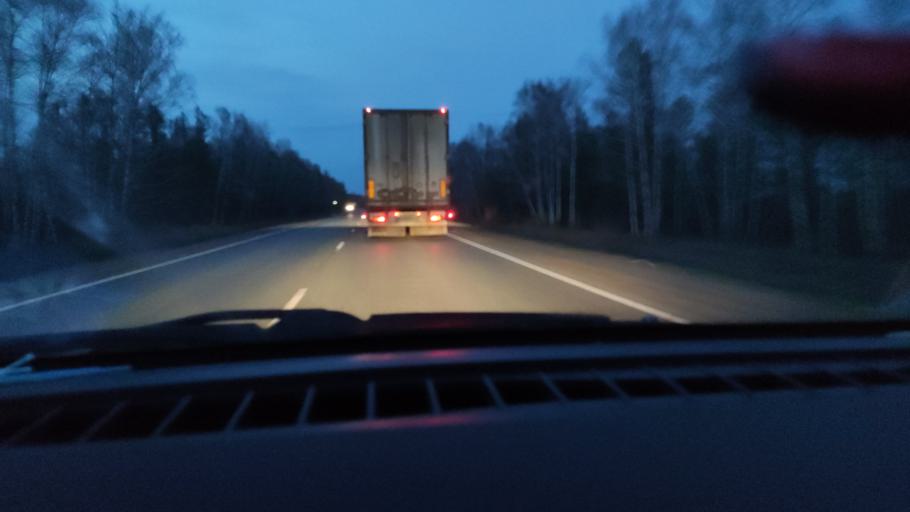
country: RU
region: Saratov
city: Sennoy
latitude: 52.1284
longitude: 46.8577
